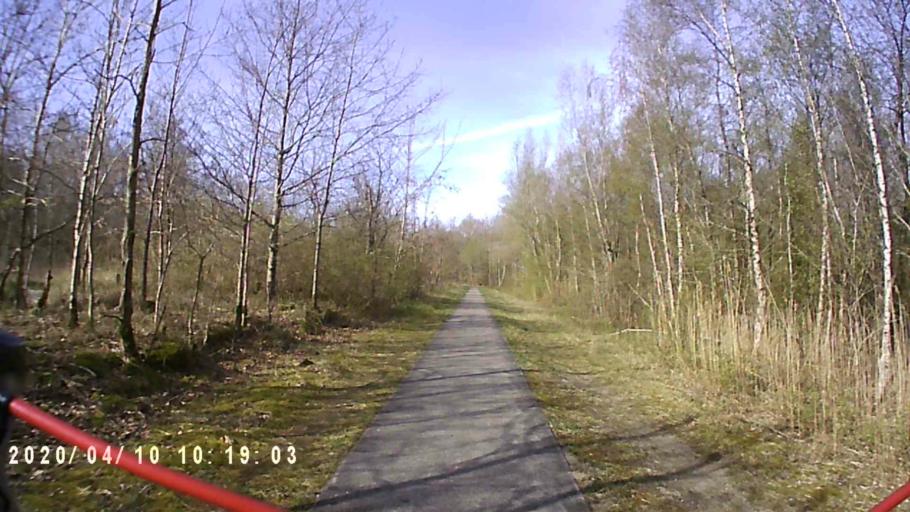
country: NL
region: Friesland
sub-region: Gemeente Dongeradeel
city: Anjum
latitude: 53.3810
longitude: 6.2264
